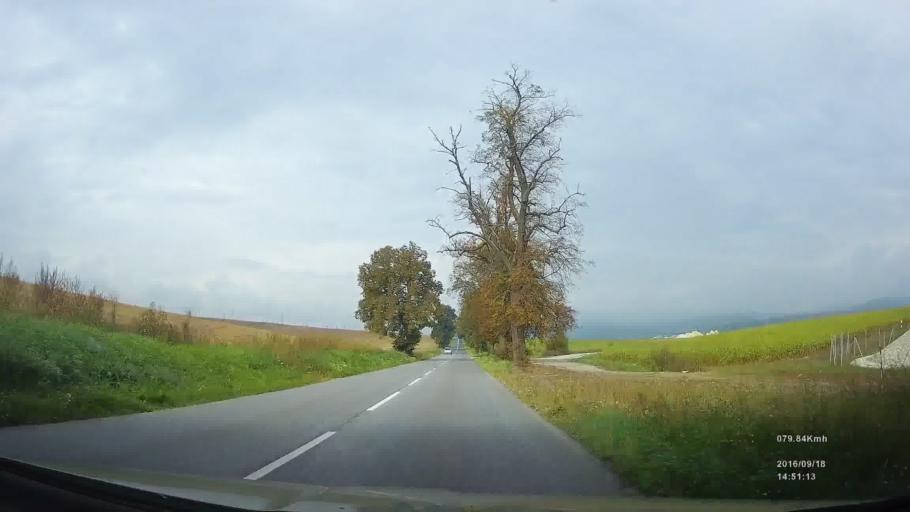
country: SK
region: Presovsky
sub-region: Okres Presov
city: Levoca
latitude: 49.0055
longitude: 20.5846
